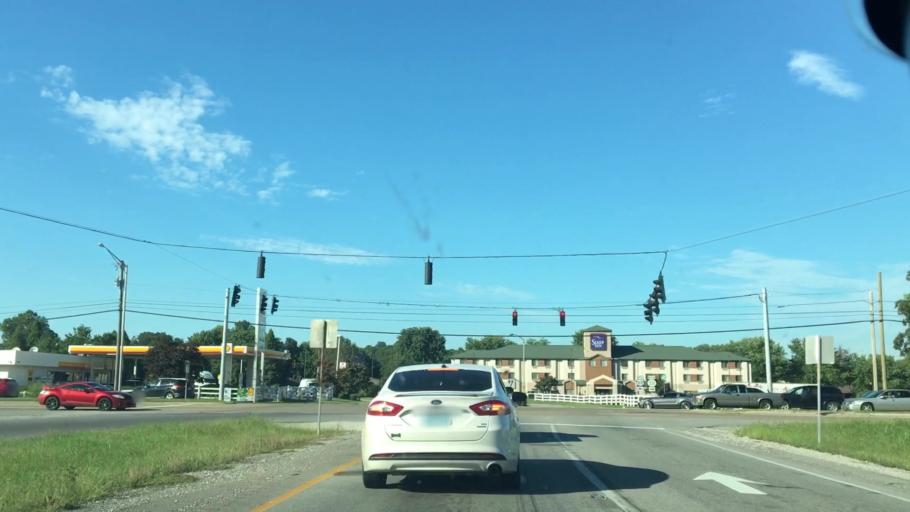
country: US
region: Kentucky
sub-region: Daviess County
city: Owensboro
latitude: 37.7747
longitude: -87.1658
